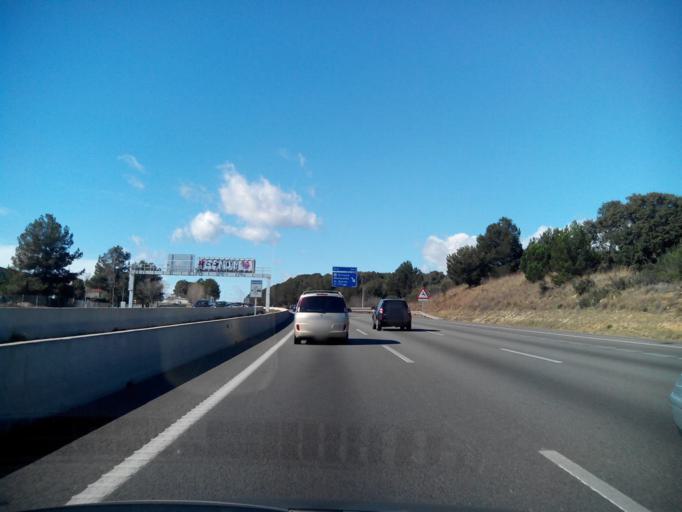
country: ES
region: Catalonia
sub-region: Provincia de Barcelona
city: Sant Quirze del Valles
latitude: 41.5431
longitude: 2.0772
